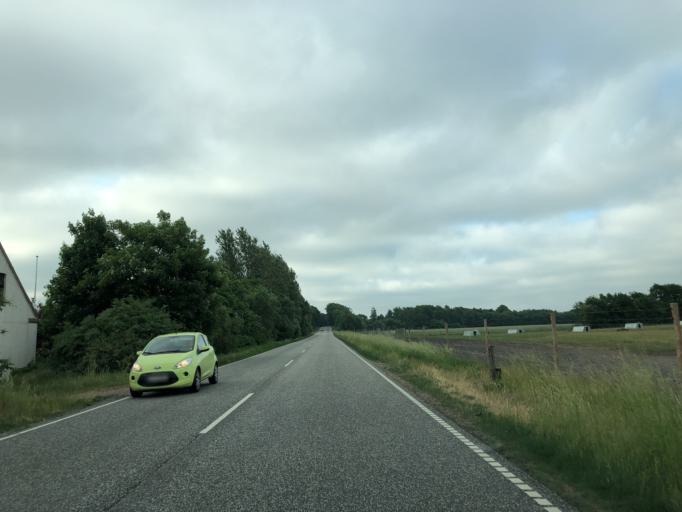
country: DK
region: South Denmark
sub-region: Vejle Kommune
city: Give
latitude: 55.8712
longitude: 9.2372
